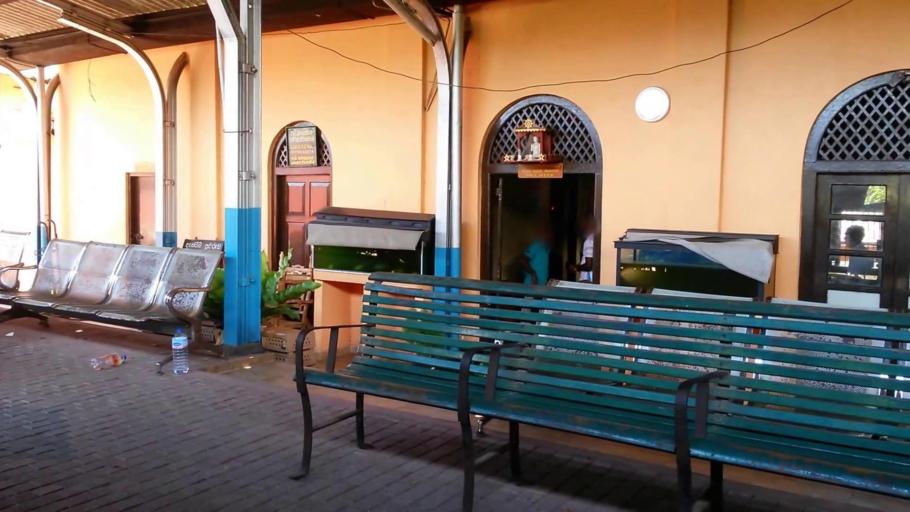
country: LK
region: Southern
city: Hikkaduwa
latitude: 6.1501
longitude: 80.0983
